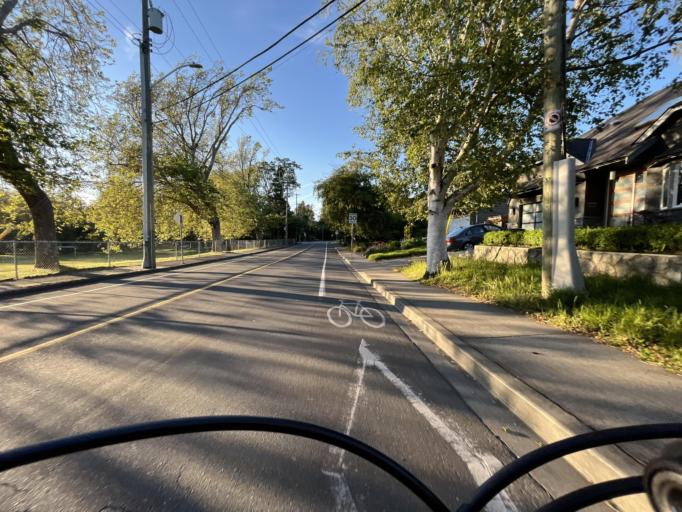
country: CA
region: British Columbia
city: Oak Bay
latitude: 48.4159
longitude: -123.3275
